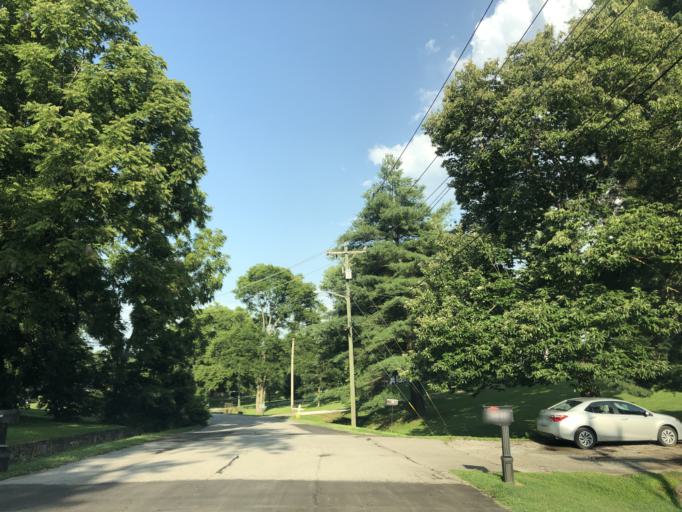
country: US
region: Tennessee
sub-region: Davidson County
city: Lakewood
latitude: 36.1521
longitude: -86.6580
